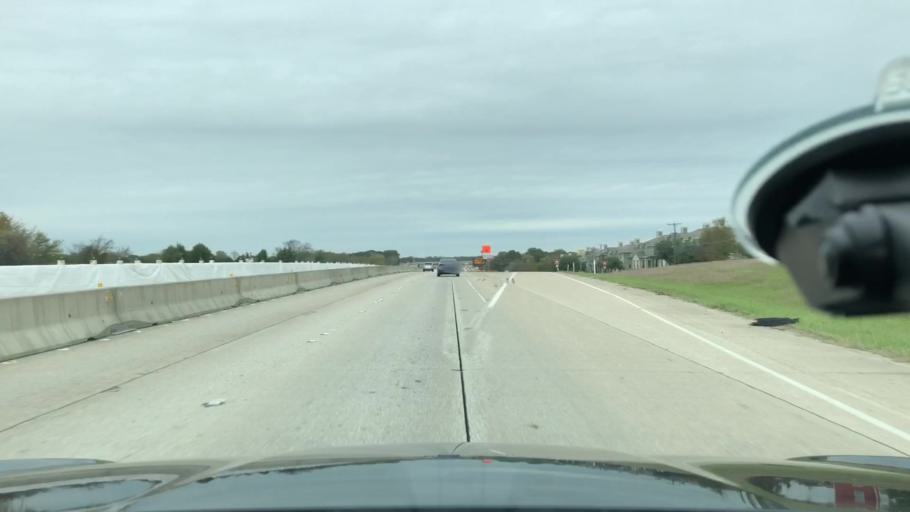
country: US
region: Texas
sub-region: Ellis County
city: Waxahachie
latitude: 32.3904
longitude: -96.8693
